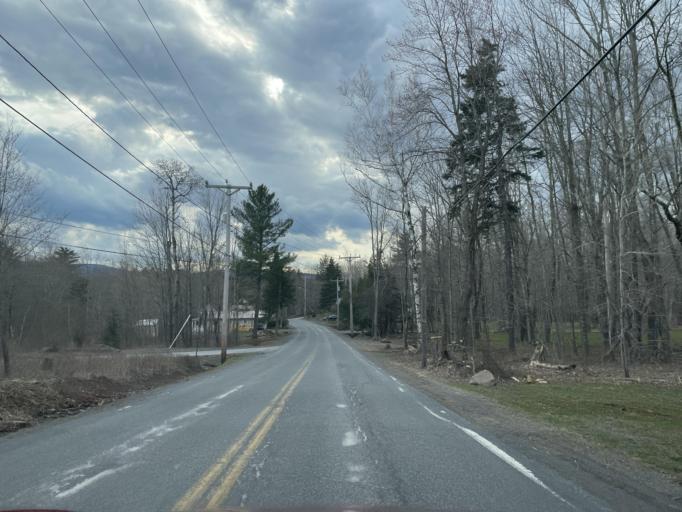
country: US
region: New York
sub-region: Greene County
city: Palenville
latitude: 42.1987
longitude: -74.0920
